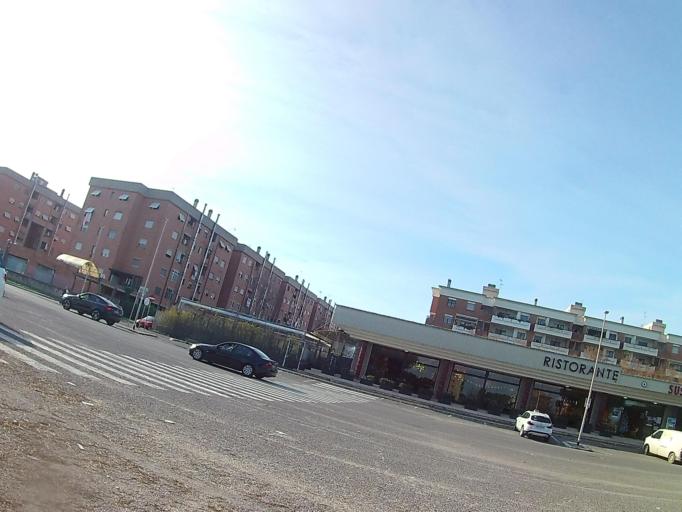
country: IT
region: Latium
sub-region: Citta metropolitana di Roma Capitale
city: Lido di Ostia
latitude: 41.7403
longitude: 12.2617
